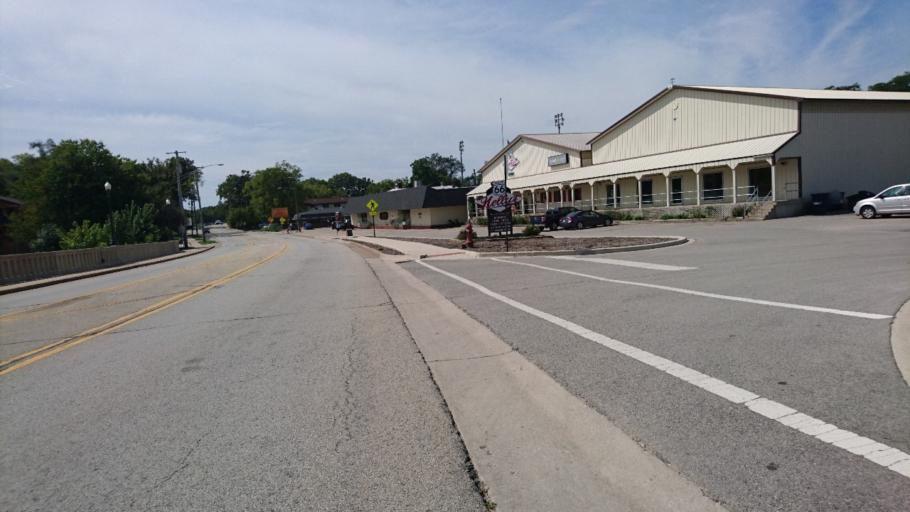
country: US
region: Illinois
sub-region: Will County
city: Wilmington
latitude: 41.3076
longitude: -88.1478
